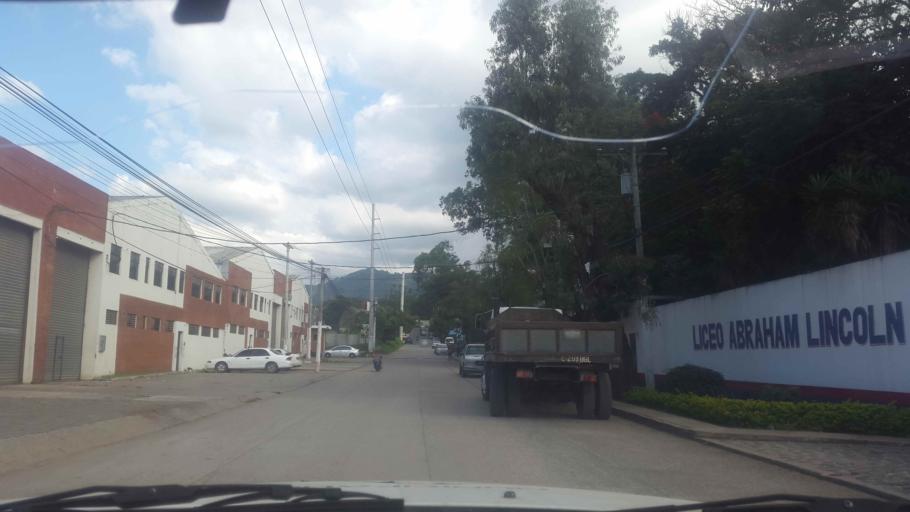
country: GT
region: Guatemala
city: Petapa
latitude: 14.5150
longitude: -90.5383
